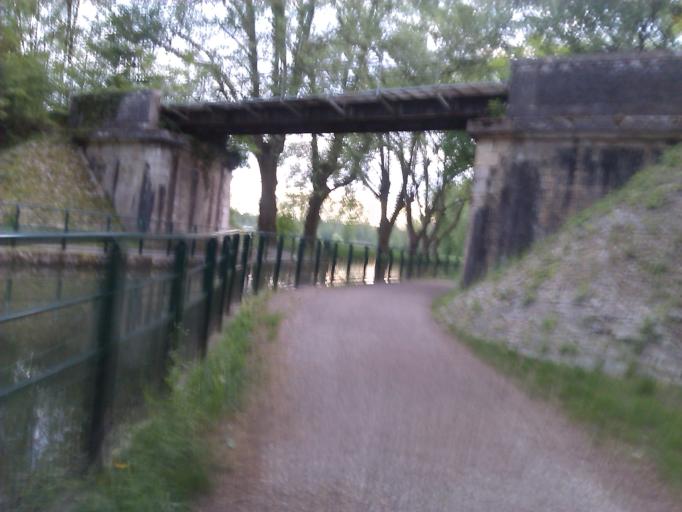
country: FR
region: Franche-Comte
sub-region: Departement du Jura
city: Dole
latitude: 47.0934
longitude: 5.5090
